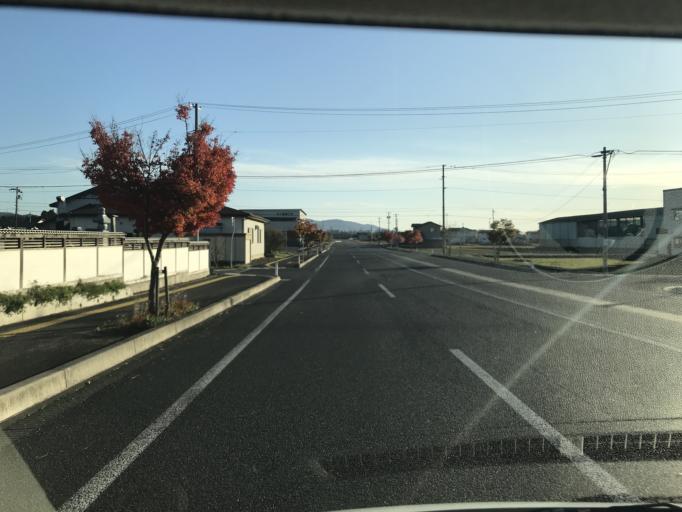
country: JP
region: Iwate
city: Mizusawa
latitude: 39.1401
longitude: 141.1838
